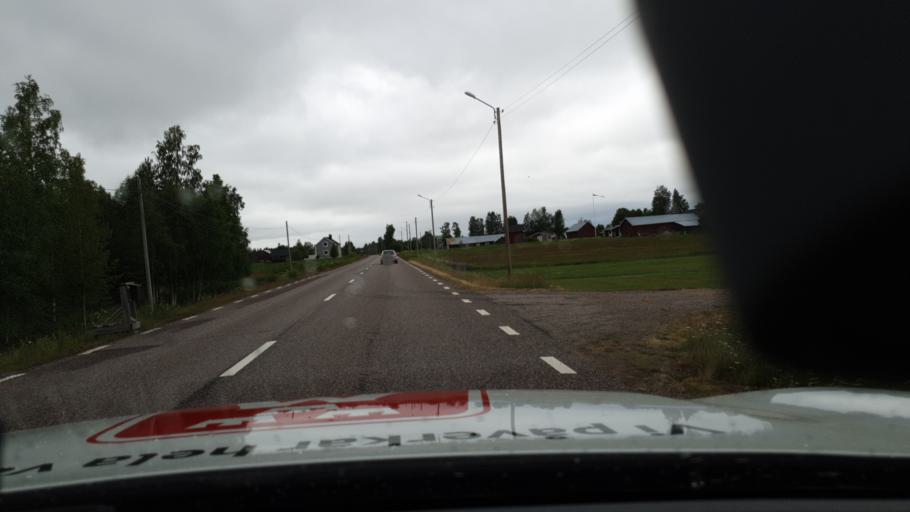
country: FI
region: Lapland
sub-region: Torniolaakso
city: Pello
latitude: 66.9806
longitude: 23.7986
